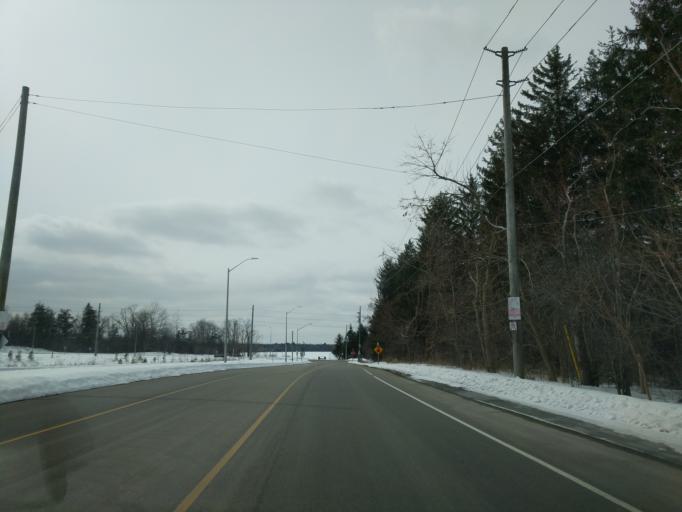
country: CA
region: Ontario
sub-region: York
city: Richmond Hill
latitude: 43.9506
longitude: -79.4259
